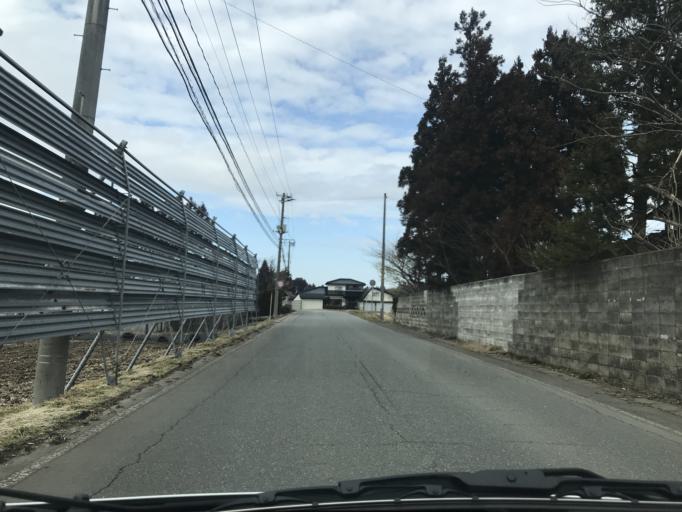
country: JP
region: Iwate
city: Kitakami
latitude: 39.3236
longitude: 140.9858
